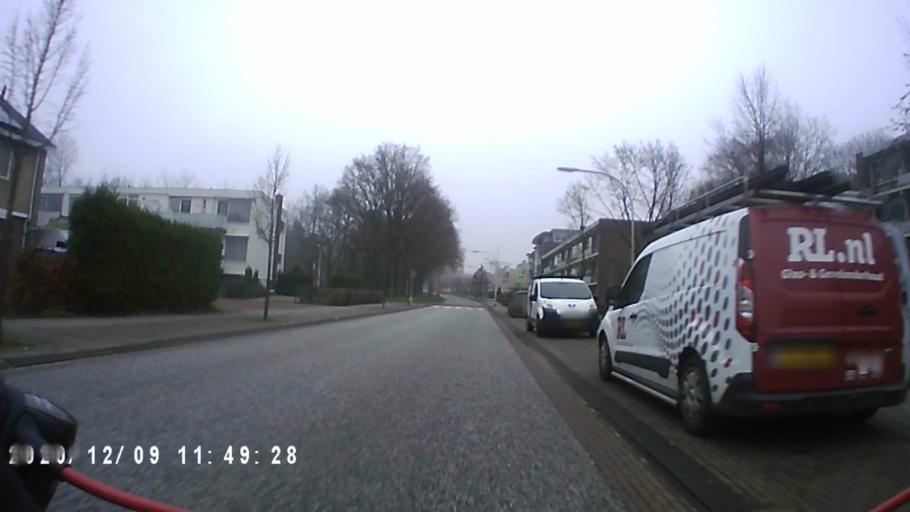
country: NL
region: Groningen
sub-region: Gemeente Haren
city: Haren
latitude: 53.1719
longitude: 6.5967
